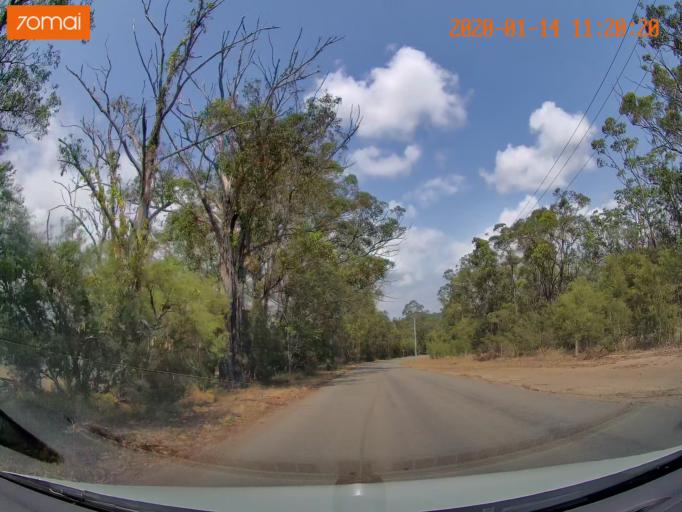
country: AU
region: New South Wales
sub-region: Lake Macquarie Shire
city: Cooranbong
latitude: -33.1013
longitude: 151.4561
